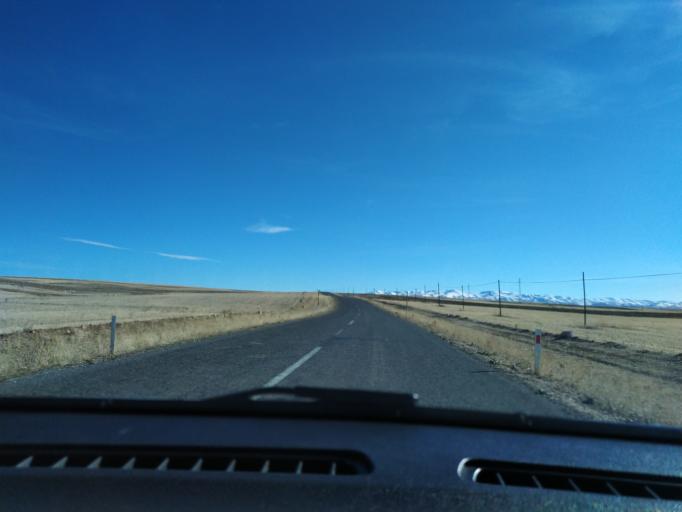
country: TR
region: Kayseri
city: Orensehir
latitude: 38.9574
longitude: 36.6849
